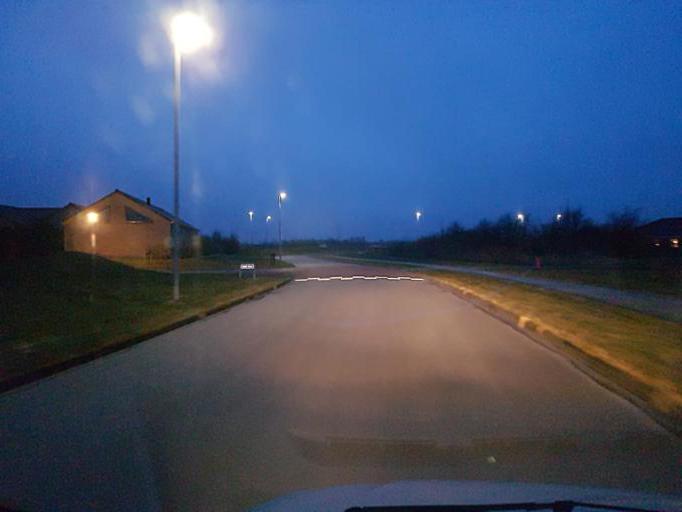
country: DK
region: South Denmark
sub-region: Esbjerg Kommune
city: Bramming
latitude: 55.4760
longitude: 8.6832
